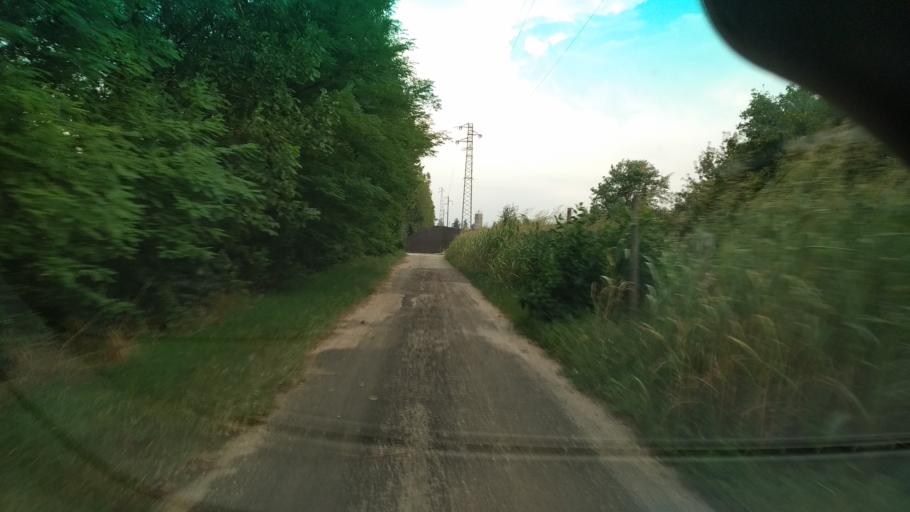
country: IT
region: Veneto
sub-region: Provincia di Vicenza
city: Montecchio Precalcino
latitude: 45.6783
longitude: 11.5636
